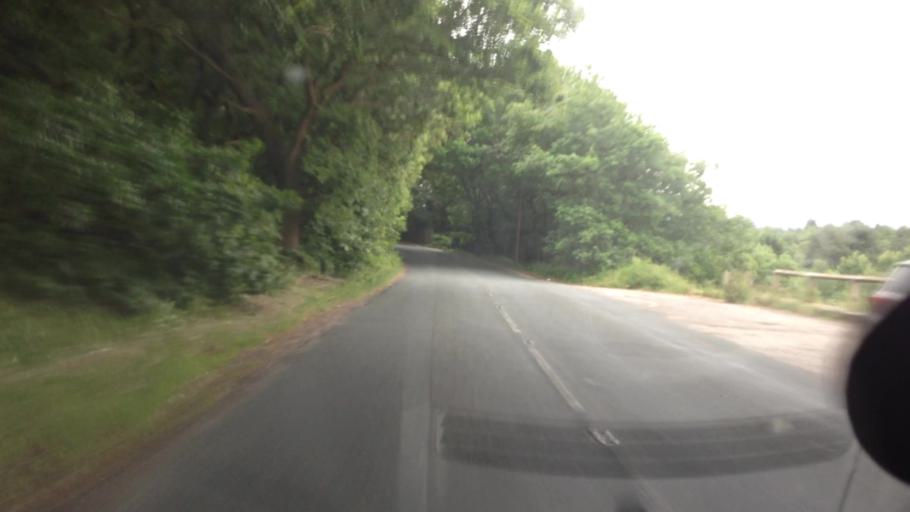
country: GB
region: England
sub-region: City and Borough of Wakefield
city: Woolley
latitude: 53.6181
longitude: -1.5393
